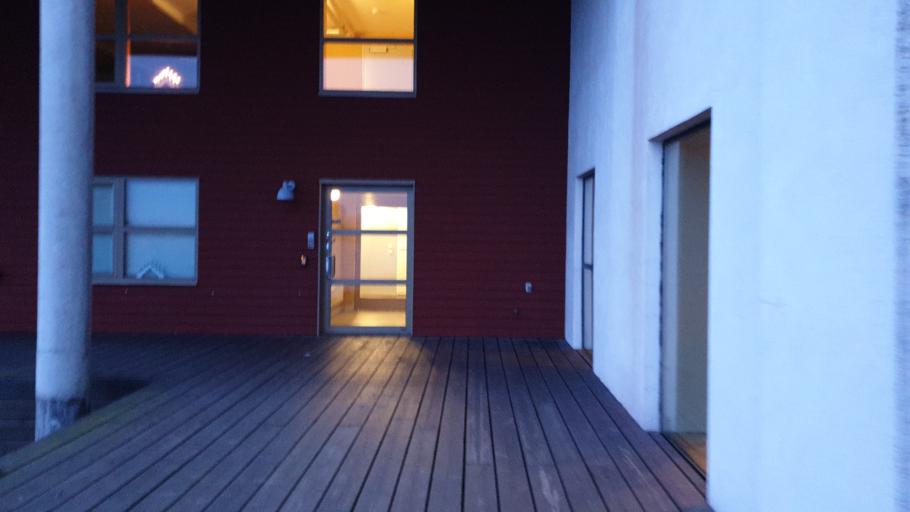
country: SE
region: Blekinge
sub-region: Karlskrona Kommun
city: Karlskrona
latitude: 56.1618
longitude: 15.5998
